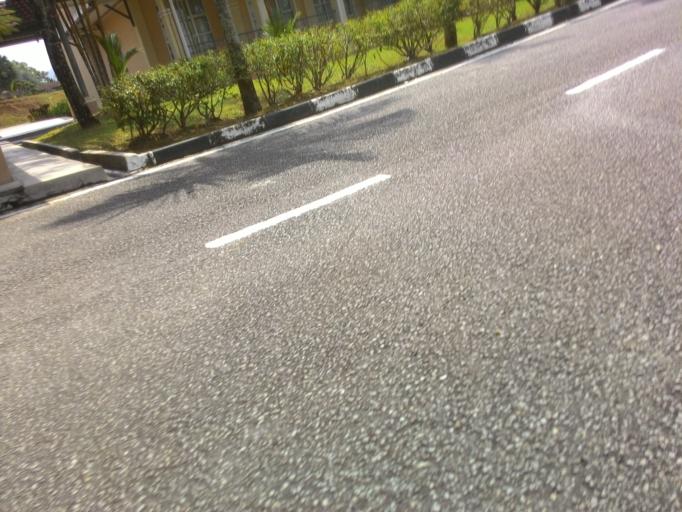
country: MY
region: Kedah
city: Kulim
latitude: 5.3836
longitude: 100.5760
